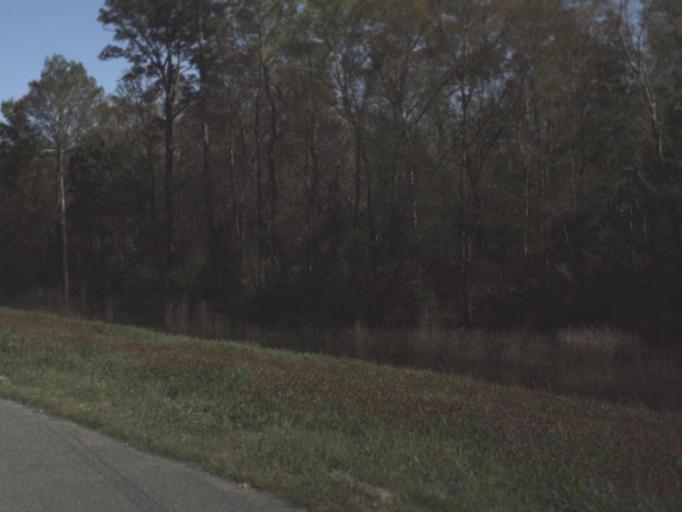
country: US
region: Florida
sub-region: Holmes County
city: Bonifay
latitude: 30.7782
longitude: -85.8369
